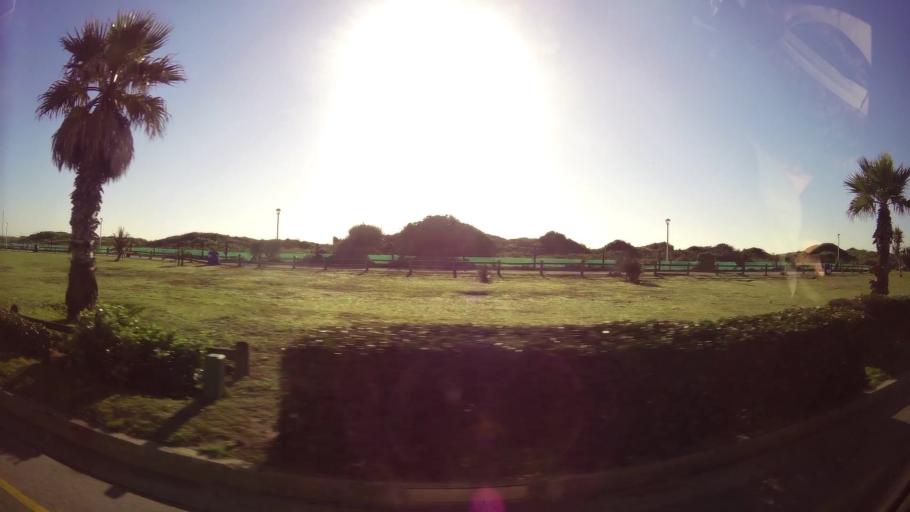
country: ZA
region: Eastern Cape
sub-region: Nelson Mandela Bay Metropolitan Municipality
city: Port Elizabeth
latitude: -33.9892
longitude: 25.6733
